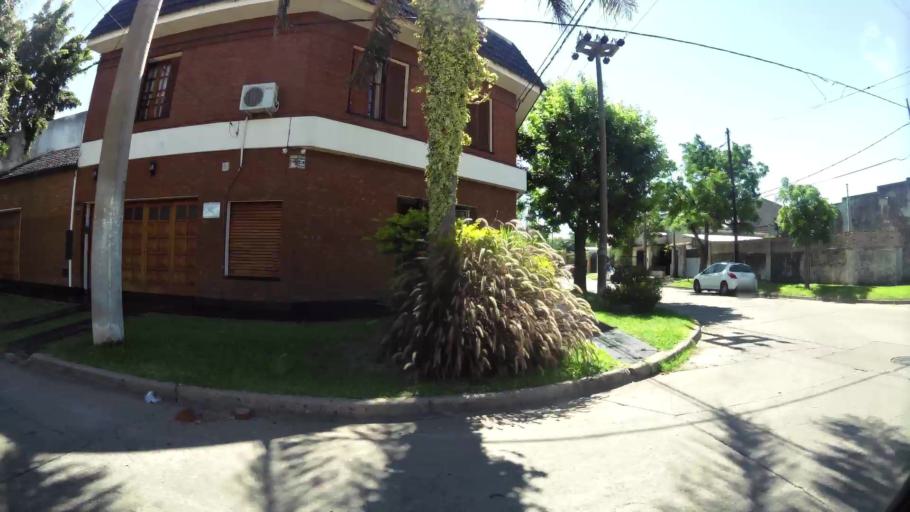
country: AR
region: Santa Fe
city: Santa Fe de la Vera Cruz
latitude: -31.6007
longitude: -60.6726
